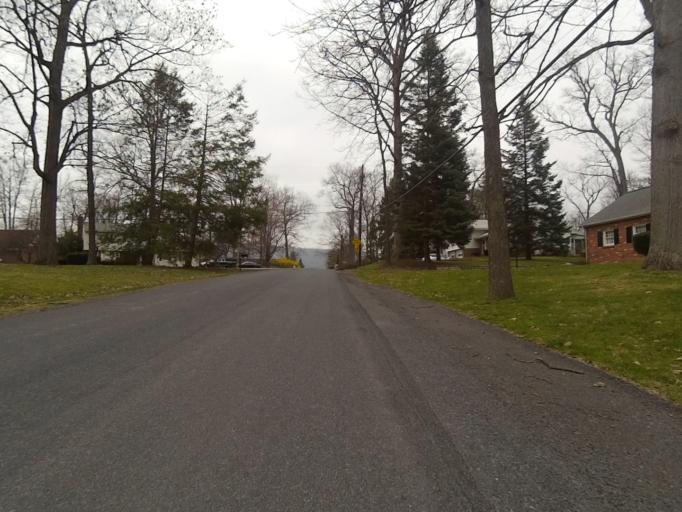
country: US
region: Pennsylvania
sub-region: Centre County
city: Boalsburg
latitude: 40.7860
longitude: -77.7730
